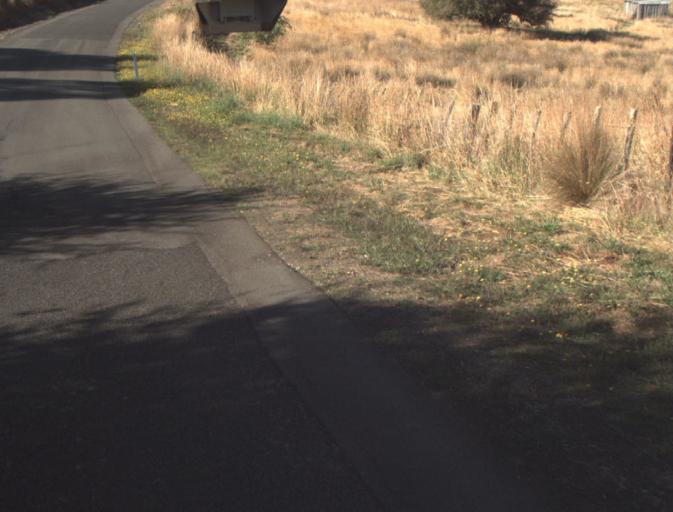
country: AU
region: Tasmania
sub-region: Launceston
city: Newstead
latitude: -41.3517
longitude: 147.3037
